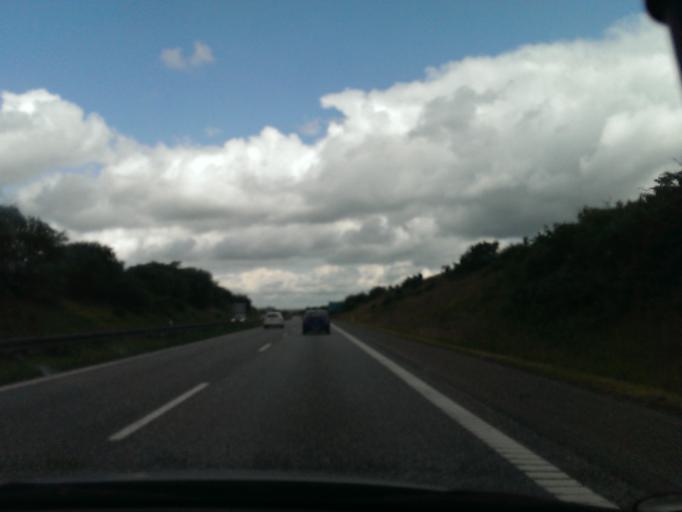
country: DK
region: North Denmark
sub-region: Mariagerfjord Kommune
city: Hobro
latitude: 56.5959
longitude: 9.7631
